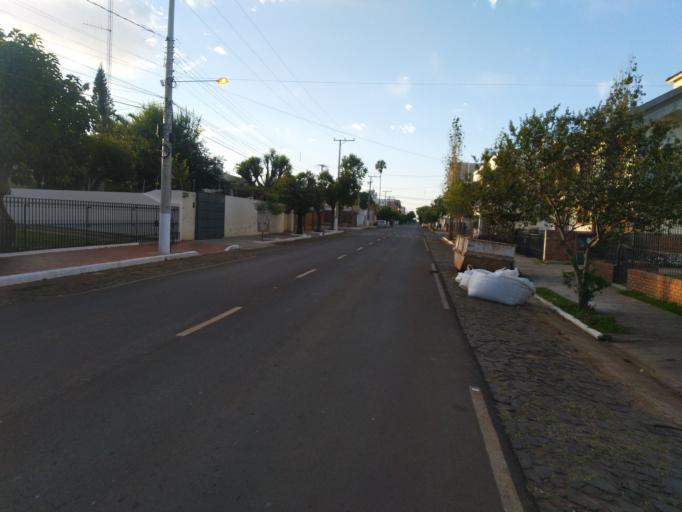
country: BR
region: Rio Grande do Sul
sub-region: Sao Borja
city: Sao Borja
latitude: -28.6565
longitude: -56.0098
